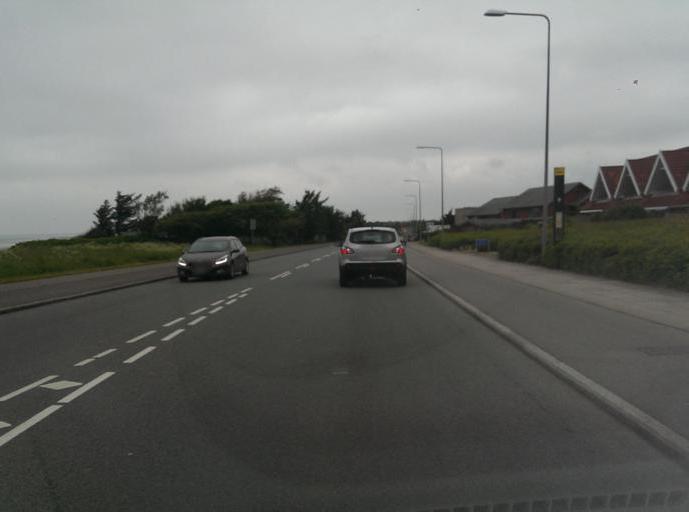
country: DK
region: South Denmark
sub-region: Fano Kommune
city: Nordby
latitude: 55.5066
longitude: 8.3832
